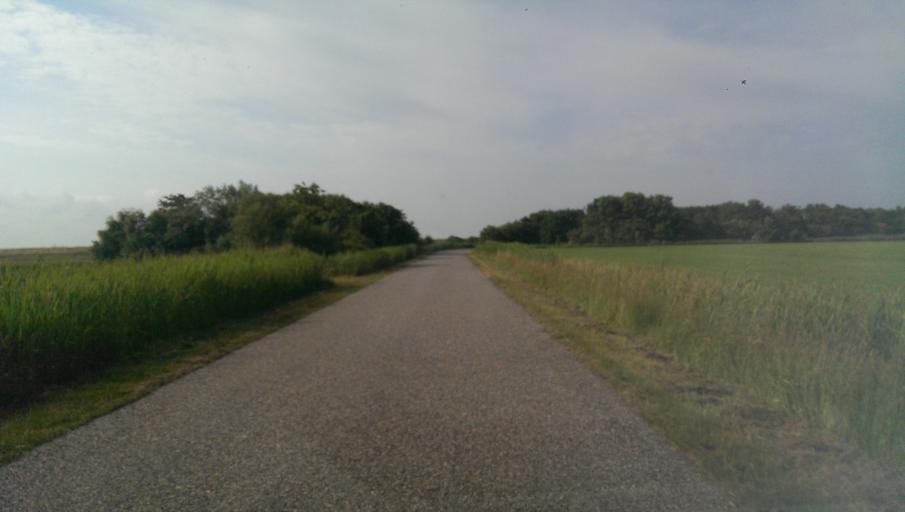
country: DK
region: South Denmark
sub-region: Esbjerg Kommune
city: Tjaereborg
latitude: 55.4360
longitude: 8.6122
